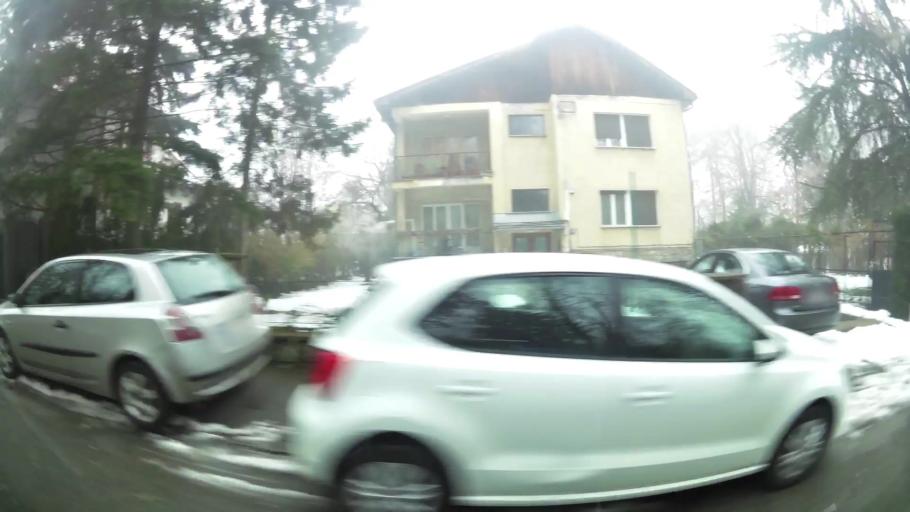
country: RS
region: Central Serbia
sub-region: Belgrade
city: Savski Venac
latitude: 44.7756
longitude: 20.4628
